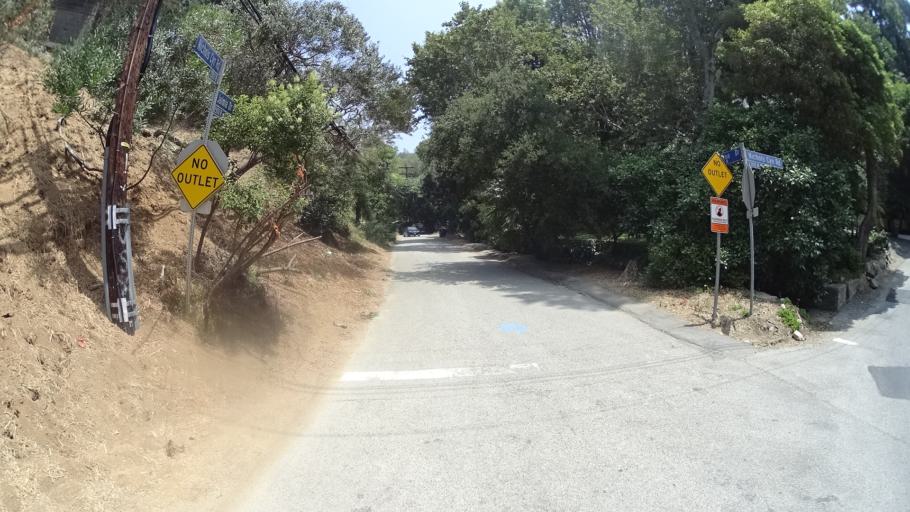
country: US
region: California
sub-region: Los Angeles County
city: Universal City
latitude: 34.1164
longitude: -118.3610
